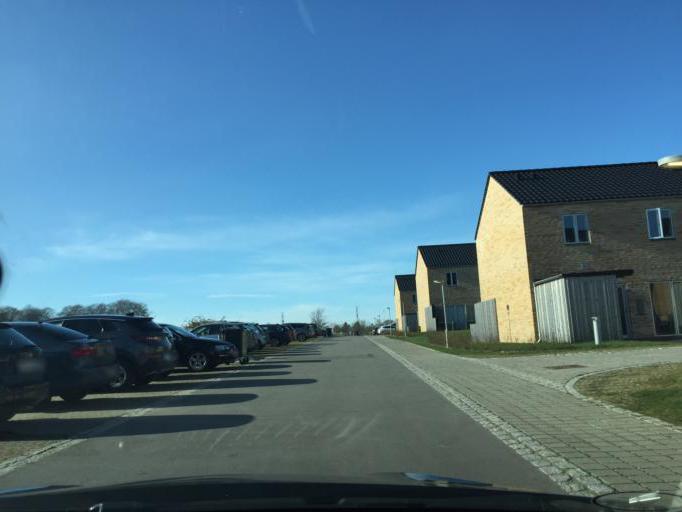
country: DK
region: South Denmark
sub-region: Odense Kommune
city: Hojby
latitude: 55.3413
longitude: 10.4215
